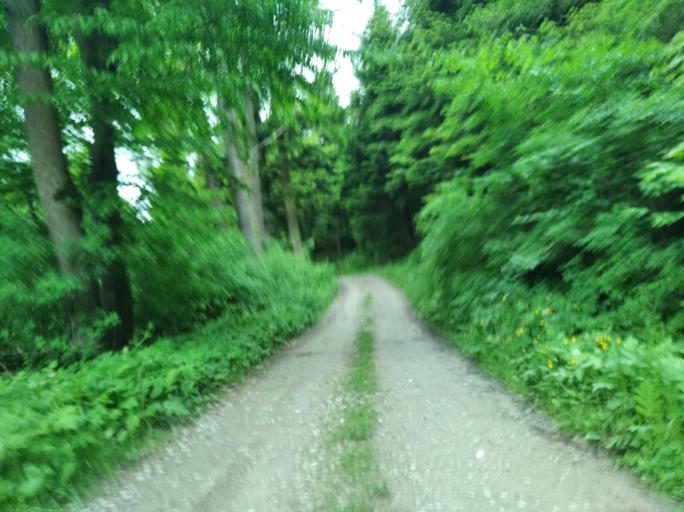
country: PL
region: Subcarpathian Voivodeship
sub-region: Powiat brzozowski
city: Jasionow
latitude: 49.6708
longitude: 21.9831
